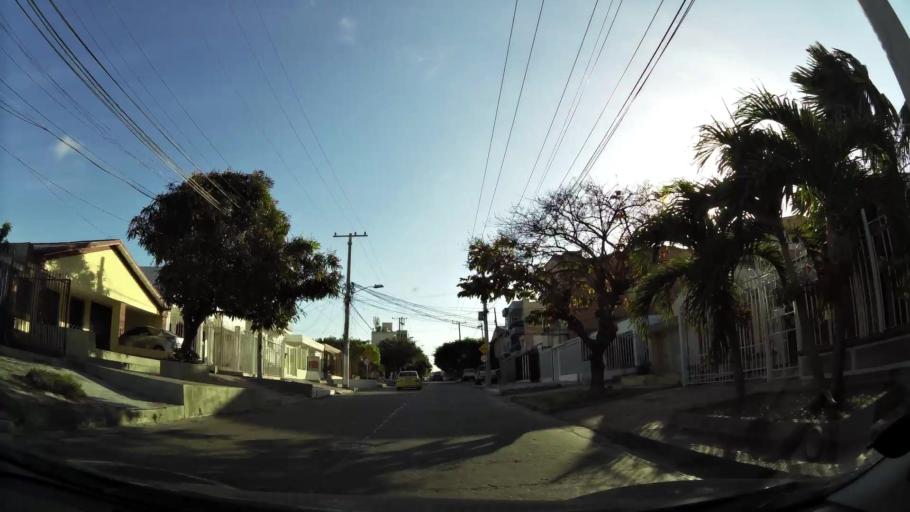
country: CO
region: Atlantico
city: Barranquilla
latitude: 10.9867
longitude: -74.8070
